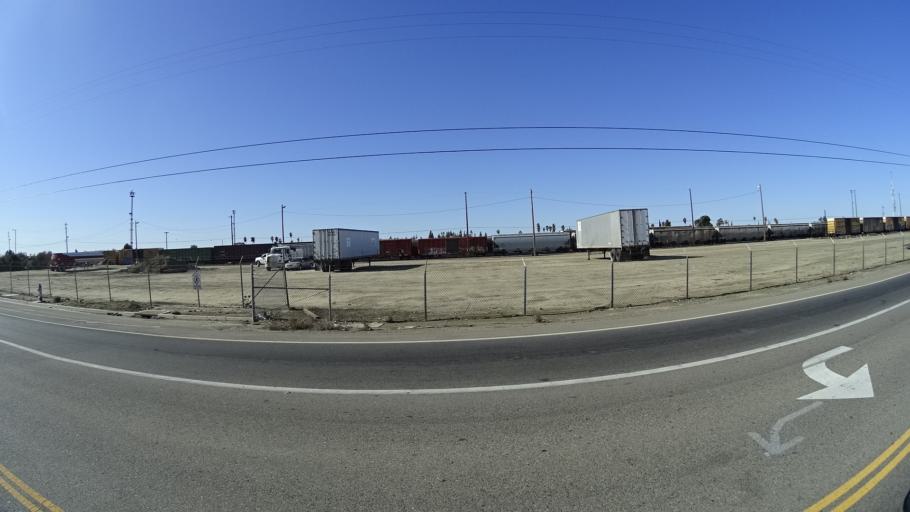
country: US
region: California
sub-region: Fresno County
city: West Park
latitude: 36.7819
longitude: -119.8448
